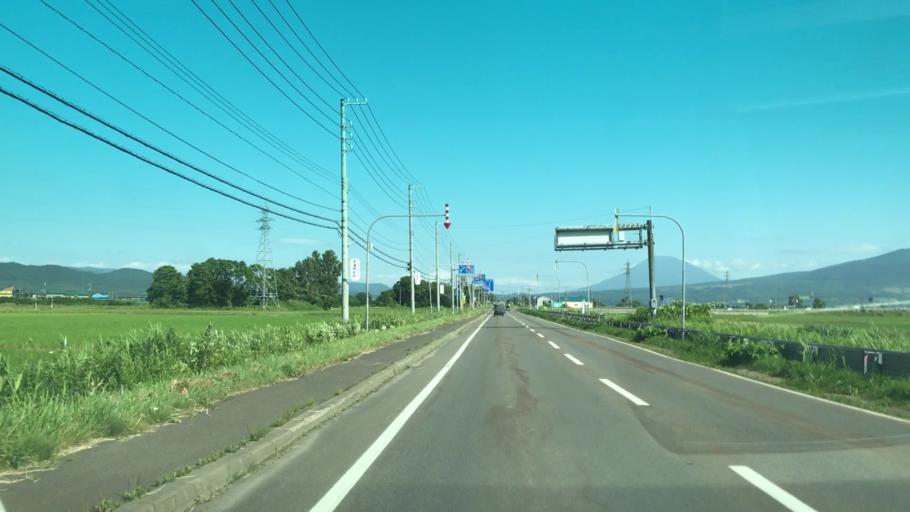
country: JP
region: Hokkaido
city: Iwanai
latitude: 43.0281
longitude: 140.5443
